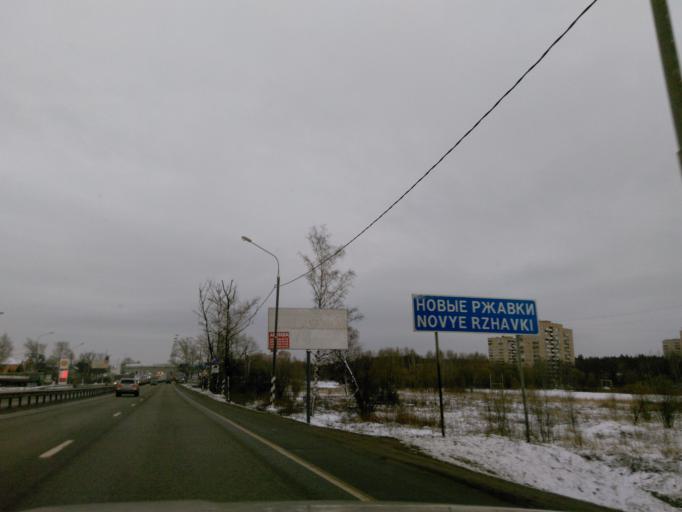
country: RU
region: Moskovskaya
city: Rzhavki
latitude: 56.0042
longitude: 37.2333
